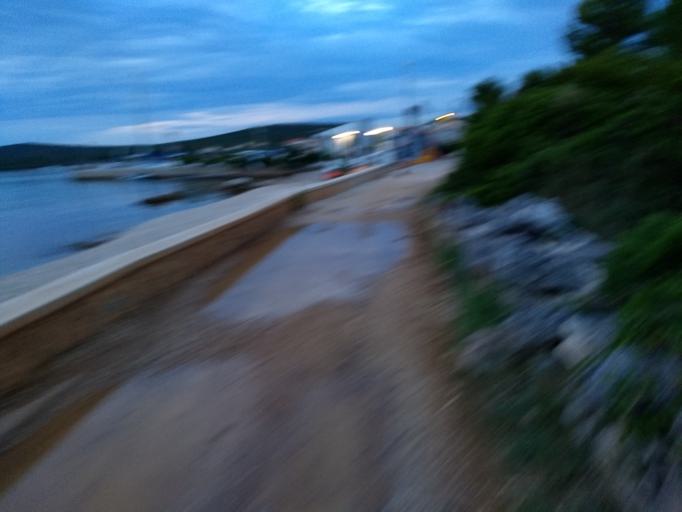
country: HR
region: Zadarska
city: Ugljan
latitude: 44.1364
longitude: 15.0705
